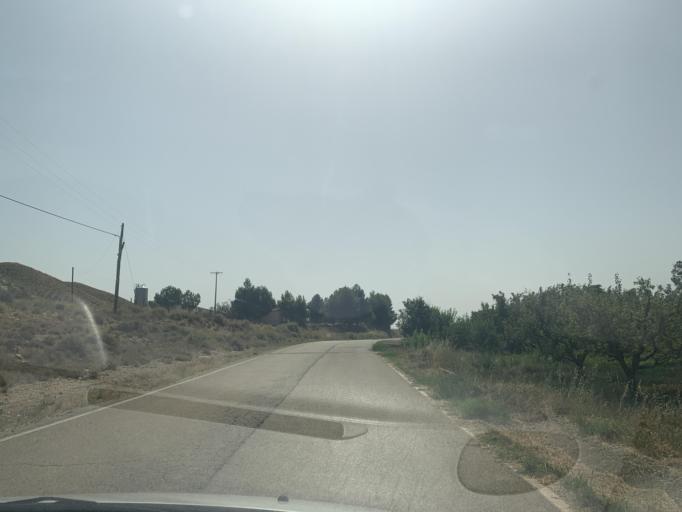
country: ES
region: Aragon
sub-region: Provincia de Zaragoza
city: Almonacid de la Cuba
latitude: 41.2739
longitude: -0.7858
